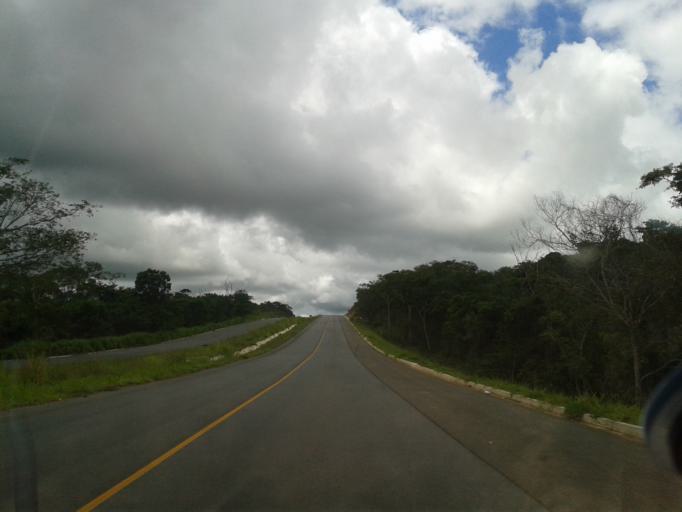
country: BR
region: Goias
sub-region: Goias
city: Goias
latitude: -16.0030
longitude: -50.0460
